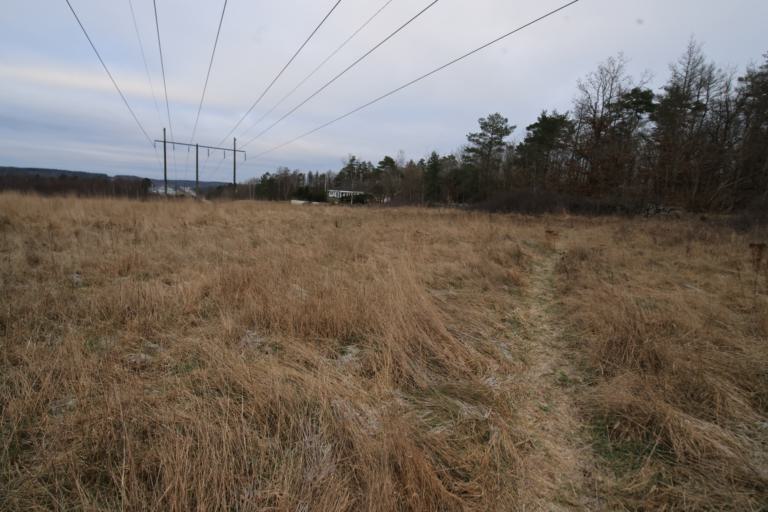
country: SE
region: Halland
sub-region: Varbergs Kommun
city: Varberg
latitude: 57.1497
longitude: 12.2923
